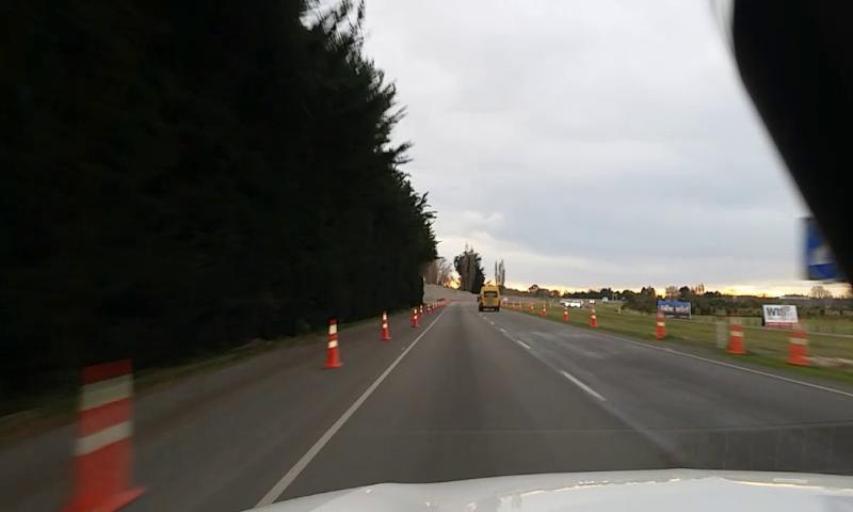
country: NZ
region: Canterbury
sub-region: Waimakariri District
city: Kaiapoi
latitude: -43.4348
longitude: 172.6392
